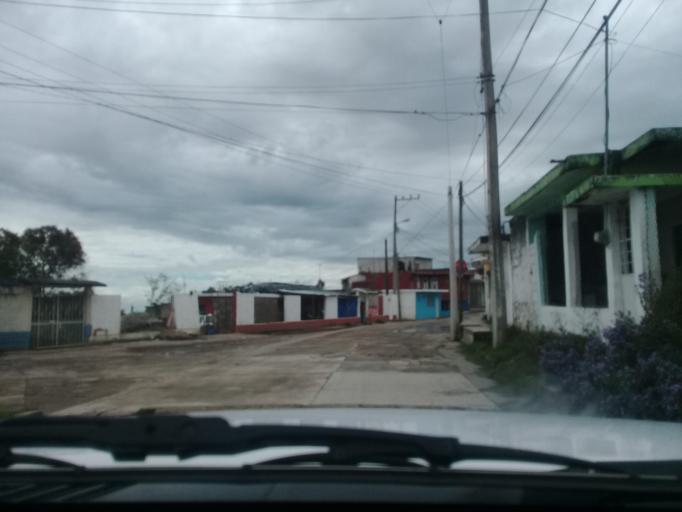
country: MX
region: Veracruz
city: Rafael Lucio
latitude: 19.5921
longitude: -96.9872
